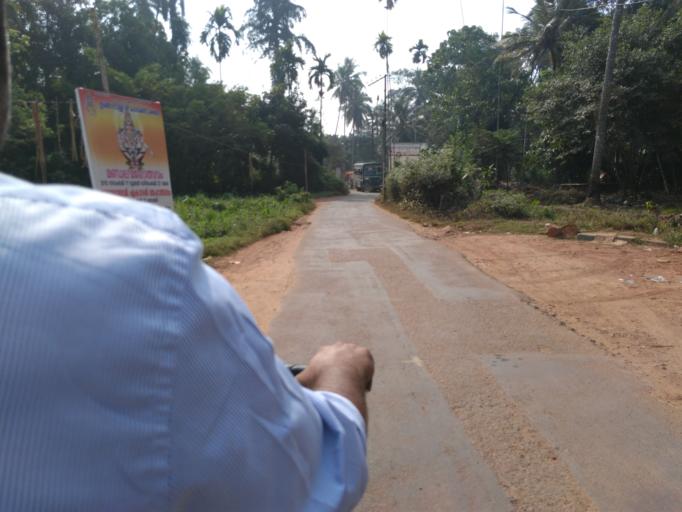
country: IN
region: Kerala
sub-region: Kozhikode
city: Kozhikode
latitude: 11.2814
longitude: 75.8255
